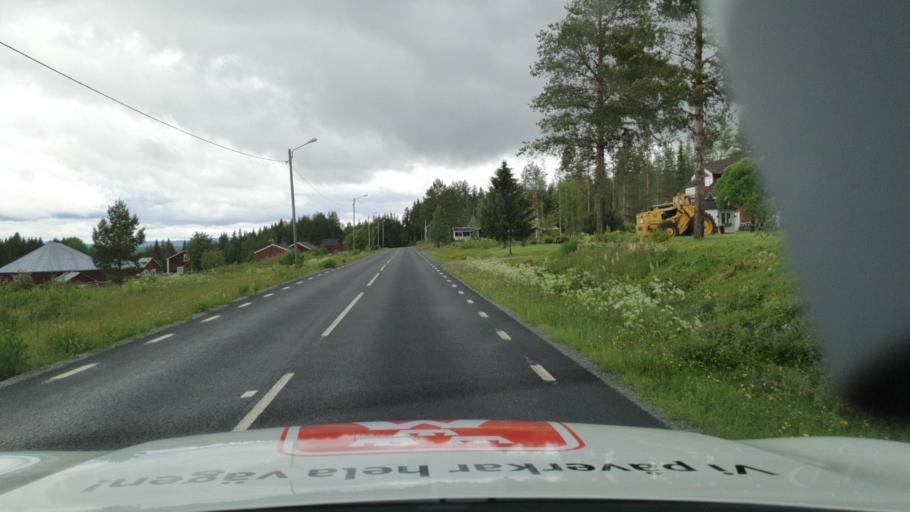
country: SE
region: Vaesterbotten
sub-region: Dorotea Kommun
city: Dorotea
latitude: 64.2355
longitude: 16.5417
